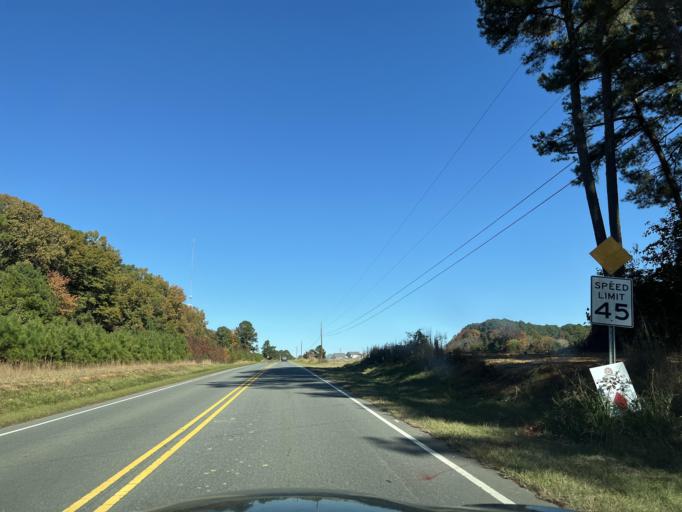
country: US
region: North Carolina
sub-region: Wake County
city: Fuquay-Varina
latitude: 35.6396
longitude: -78.7255
